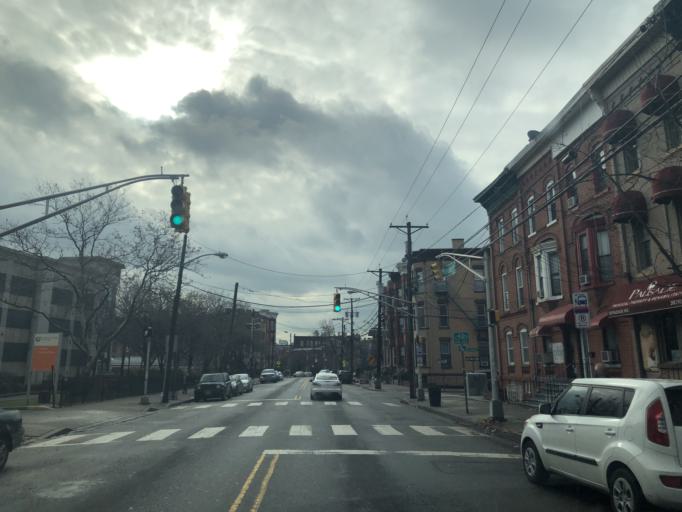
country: US
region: New Jersey
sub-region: Hudson County
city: Hoboken
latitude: 40.7339
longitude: -74.0508
